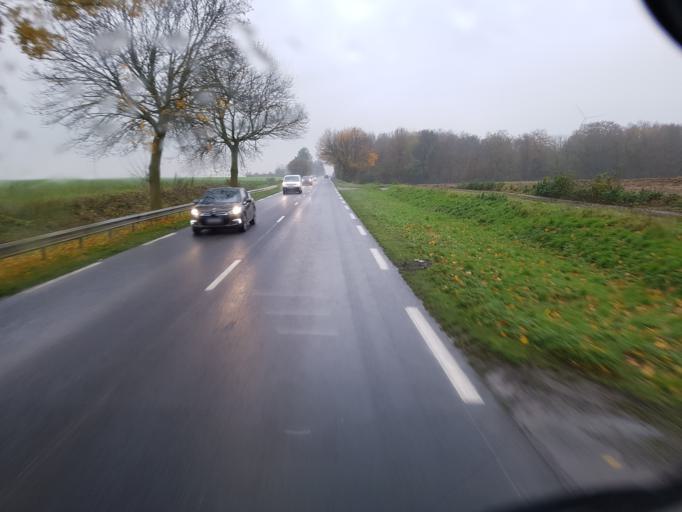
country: FR
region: Picardie
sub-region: Departement de l'Aisne
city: Saint-Quentin
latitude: 49.8826
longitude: 3.2672
